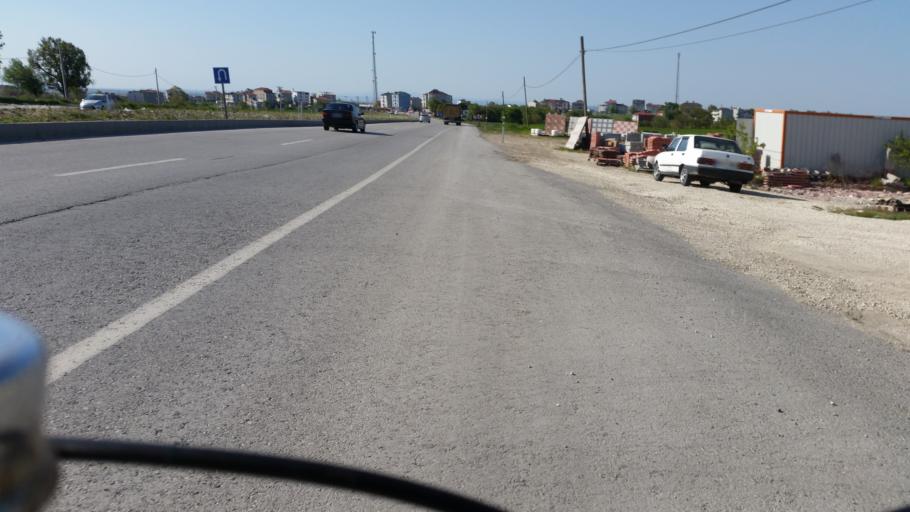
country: TR
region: Tekirdag
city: Cerkezkoey
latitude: 41.3514
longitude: 27.9573
